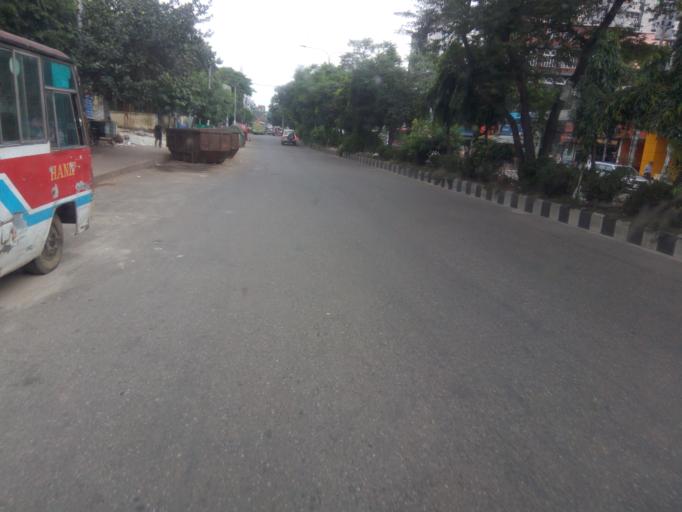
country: BD
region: Dhaka
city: Azimpur
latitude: 23.7502
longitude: 90.3789
